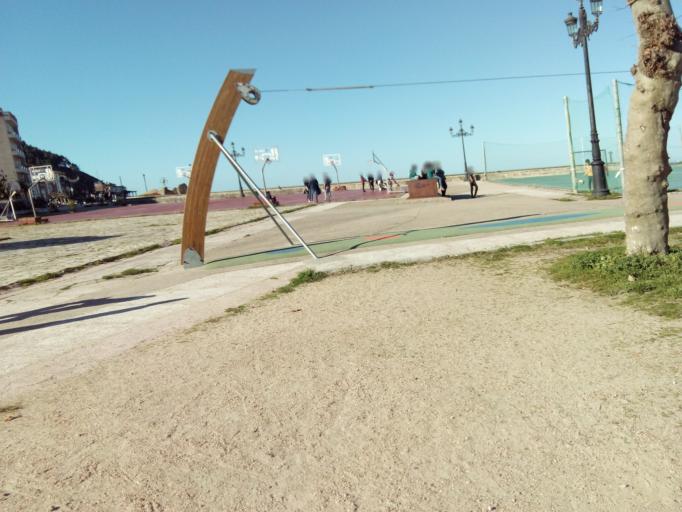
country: ES
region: Galicia
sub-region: Provincia de Pontevedra
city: Baiona
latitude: 42.1220
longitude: -8.8507
